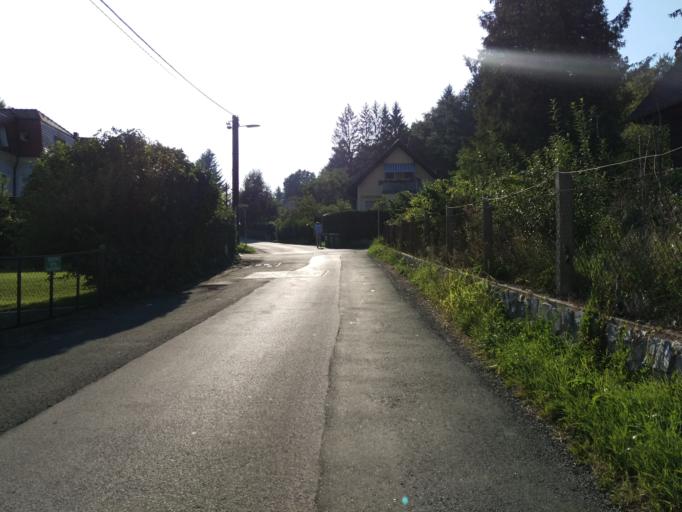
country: AT
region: Styria
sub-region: Graz Stadt
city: Mariatrost
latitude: 47.0738
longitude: 15.4981
